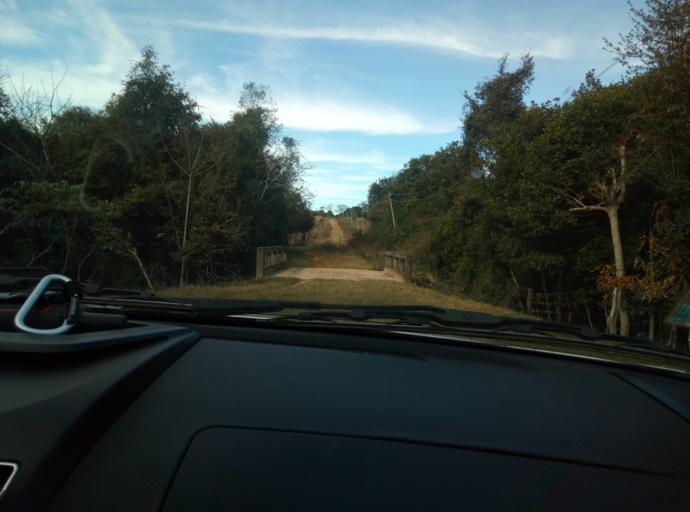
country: PY
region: Caaguazu
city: Carayao
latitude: -25.1717
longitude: -56.2902
